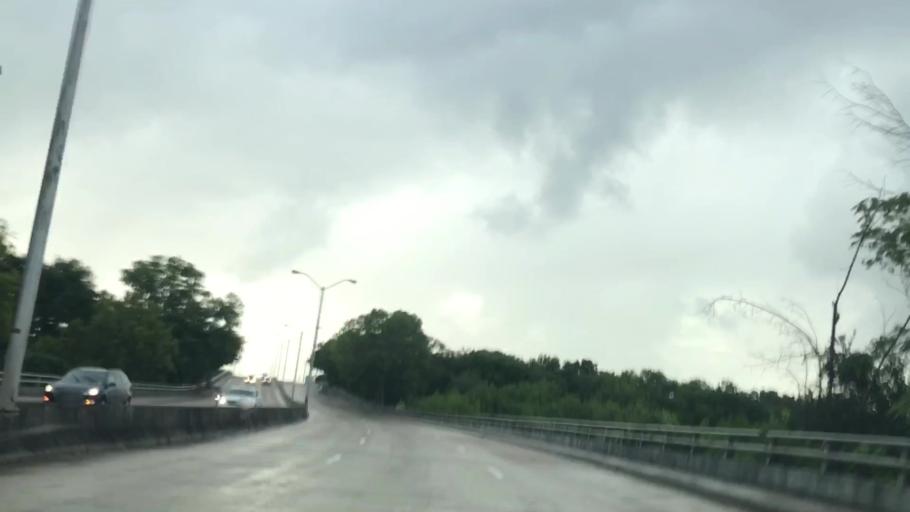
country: US
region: Texas
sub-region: Dallas County
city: Richardson
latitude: 32.8986
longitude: -96.7625
